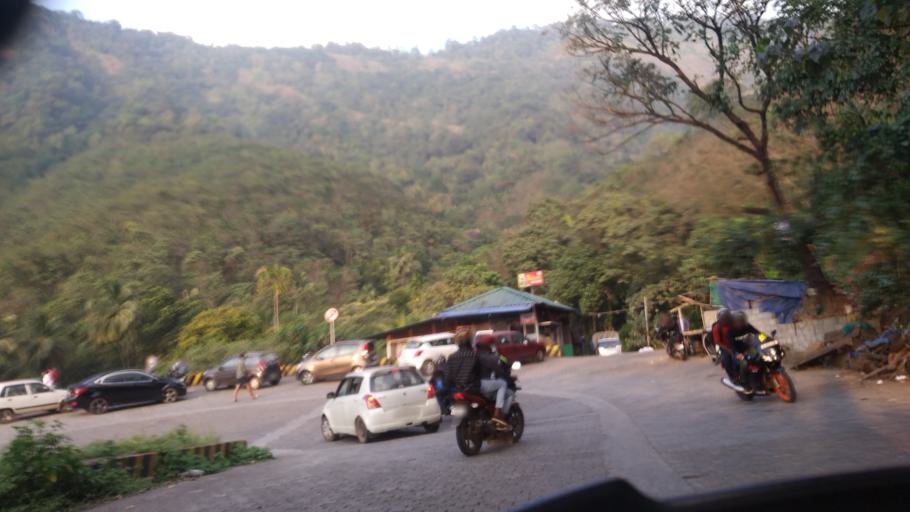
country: IN
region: Kerala
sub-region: Wayanad
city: Kalpetta
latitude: 11.5034
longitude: 76.0239
